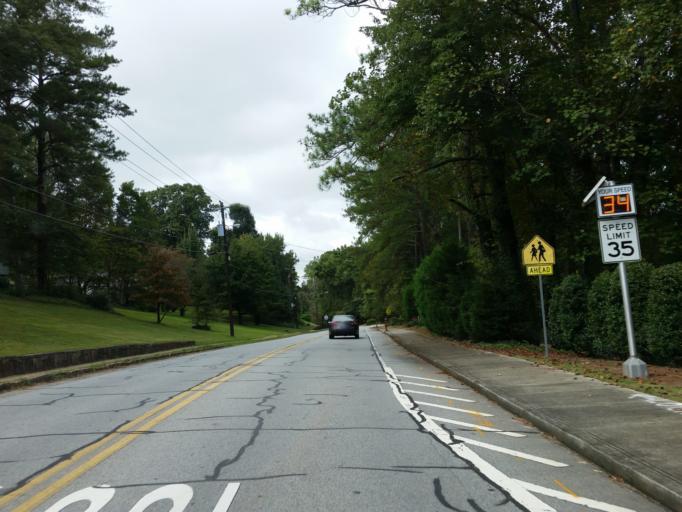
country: US
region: Georgia
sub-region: DeKalb County
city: Dunwoody
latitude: 33.9560
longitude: -84.3402
